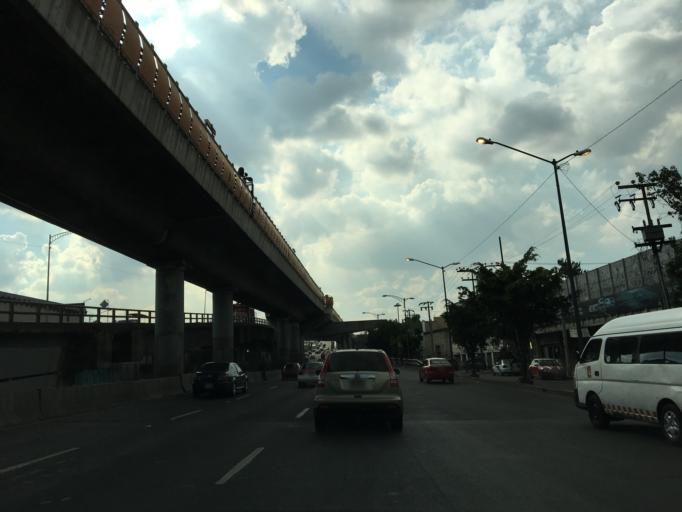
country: MX
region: Mexico City
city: Venustiano Carranza
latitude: 19.4359
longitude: -99.1056
